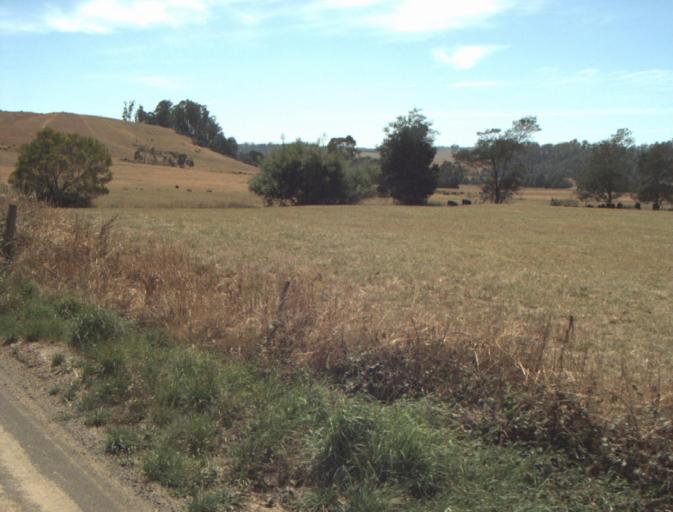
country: AU
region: Tasmania
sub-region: Launceston
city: Mayfield
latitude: -41.2558
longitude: 147.1328
